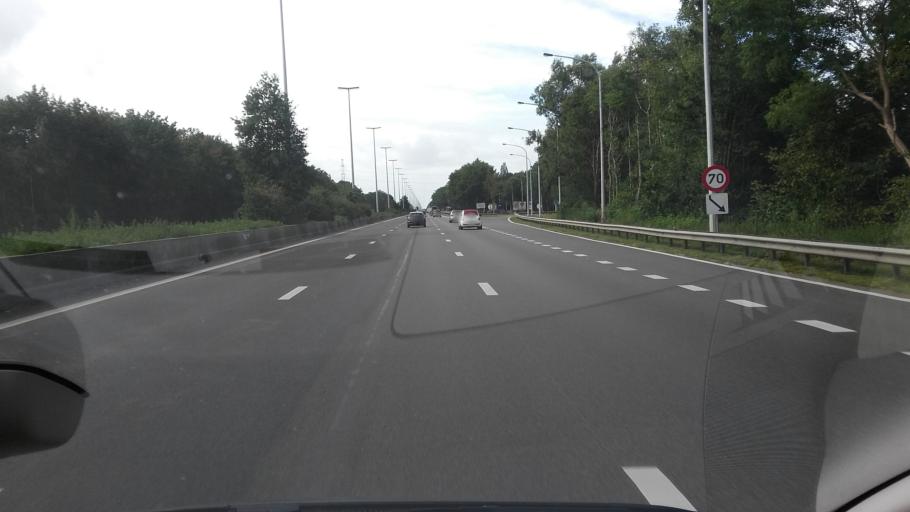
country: BE
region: Wallonia
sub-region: Province de Liege
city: Fexhe-le-Haut-Clocher
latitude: 50.6864
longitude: 5.4221
